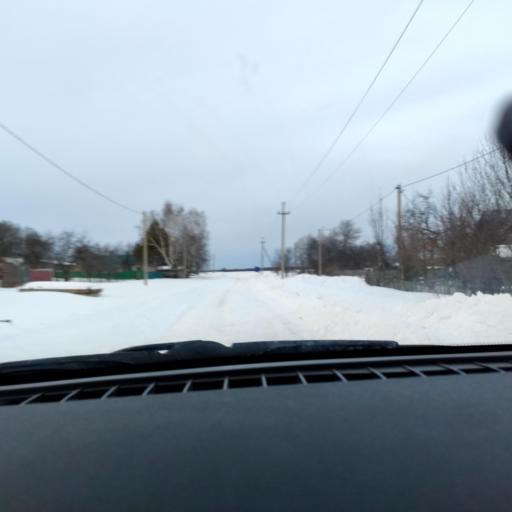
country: RU
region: Bashkortostan
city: Iglino
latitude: 54.7377
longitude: 56.5391
